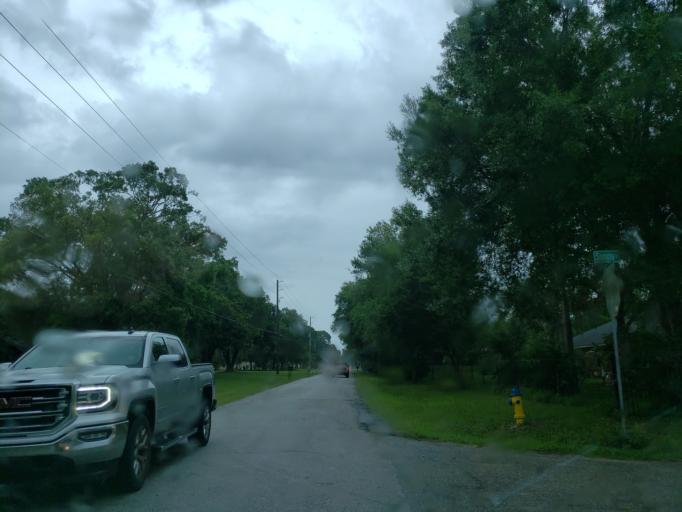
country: US
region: Florida
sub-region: Pasco County
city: Wesley Chapel
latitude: 28.2647
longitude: -82.3496
